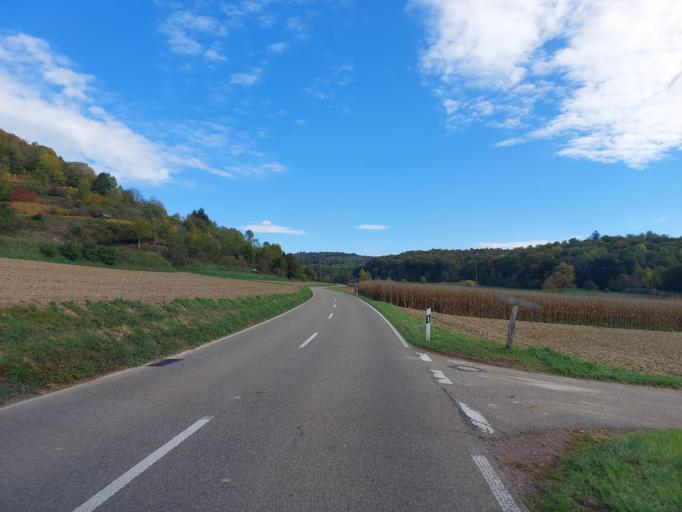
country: DE
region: Baden-Wuerttemberg
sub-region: Freiburg Region
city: Malterdingen
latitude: 48.1696
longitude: 7.8078
